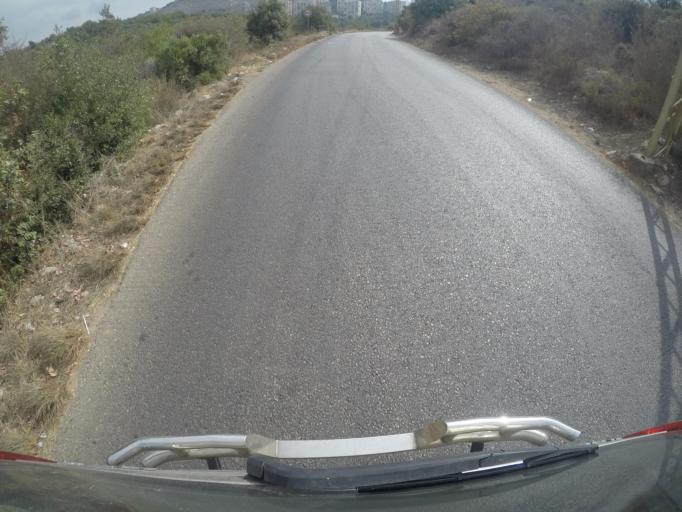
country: LB
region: Mont-Liban
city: Beit ed Dine
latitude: 33.7373
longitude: 35.4823
